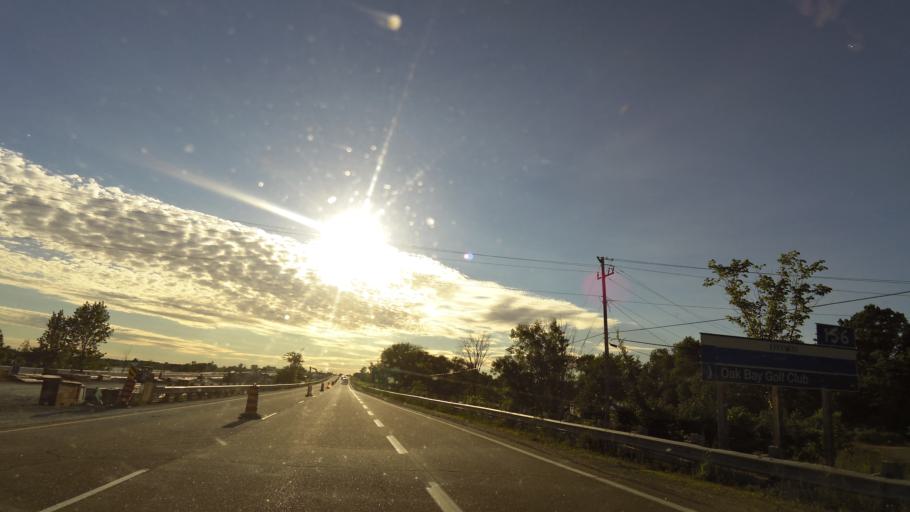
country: CA
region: Ontario
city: Midland
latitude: 44.7988
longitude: -79.7171
